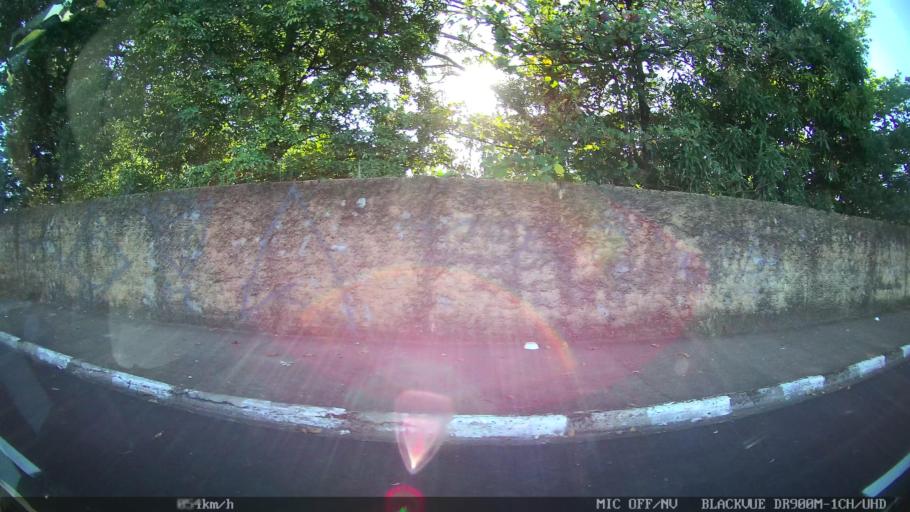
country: BR
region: Sao Paulo
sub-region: Franca
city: Franca
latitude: -20.5674
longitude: -47.3953
